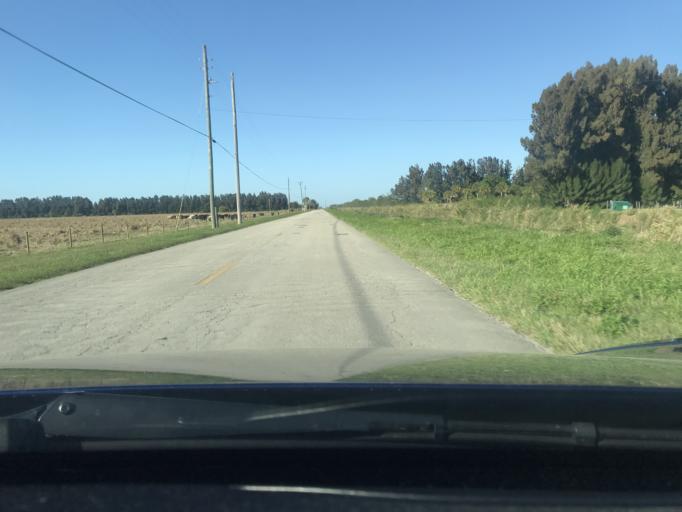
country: US
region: Florida
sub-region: Saint Lucie County
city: Lakewood Park
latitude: 27.4231
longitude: -80.4975
